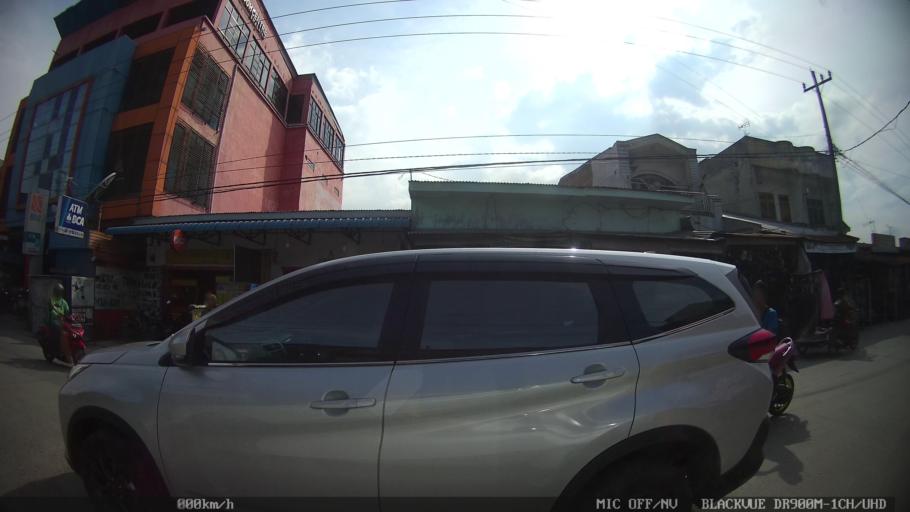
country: ID
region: North Sumatra
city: Medan
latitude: 3.5951
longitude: 98.7538
